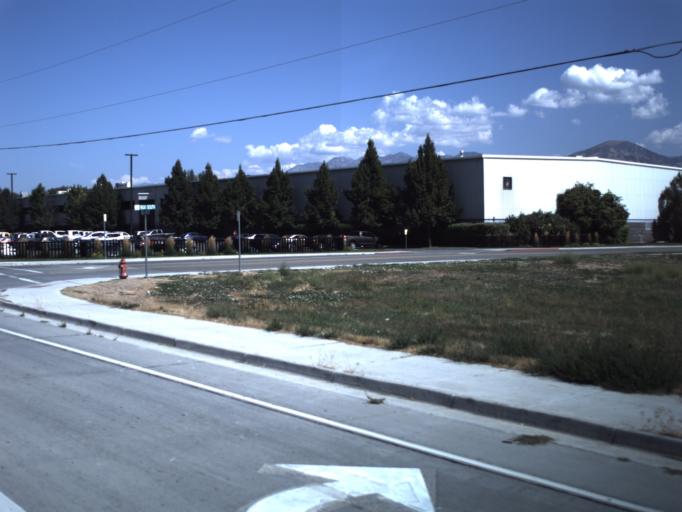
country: US
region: Utah
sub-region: Cache County
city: Nibley
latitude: 41.7033
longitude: -111.8603
